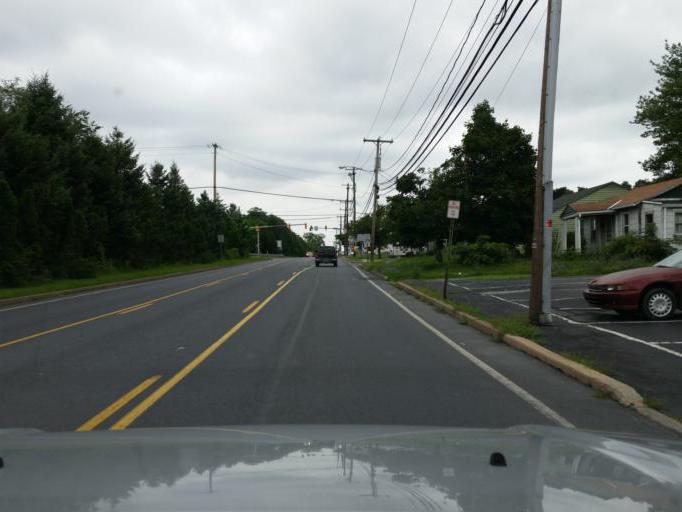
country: US
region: Pennsylvania
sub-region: Dauphin County
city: Rutherford
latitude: 40.2642
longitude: -76.7765
